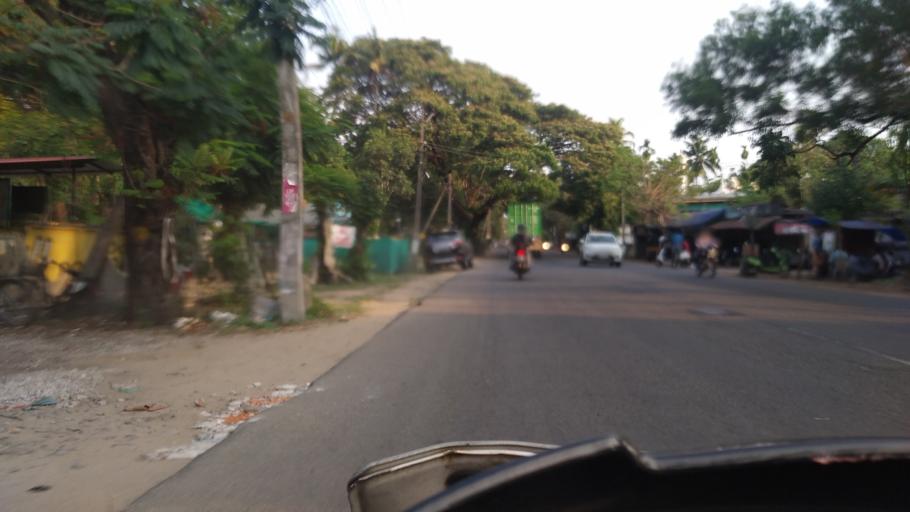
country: IN
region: Kerala
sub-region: Thrissur District
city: Irinjalakuda
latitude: 10.3299
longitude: 76.1415
